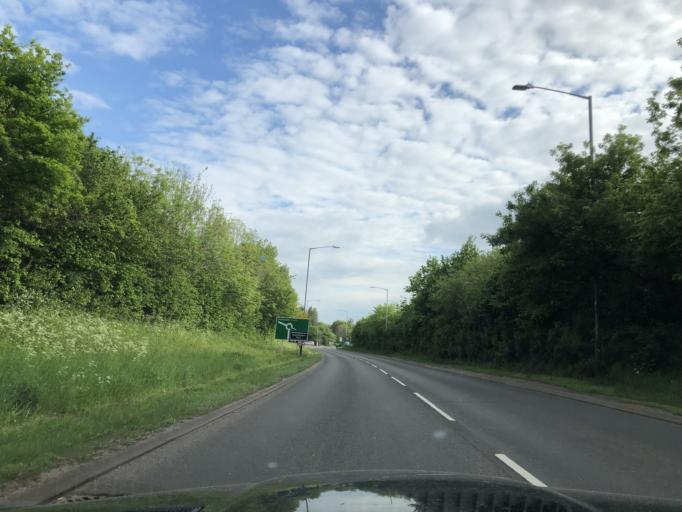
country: GB
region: England
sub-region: Warwickshire
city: Wellesbourne Mountford
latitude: 52.1938
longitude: -1.6039
